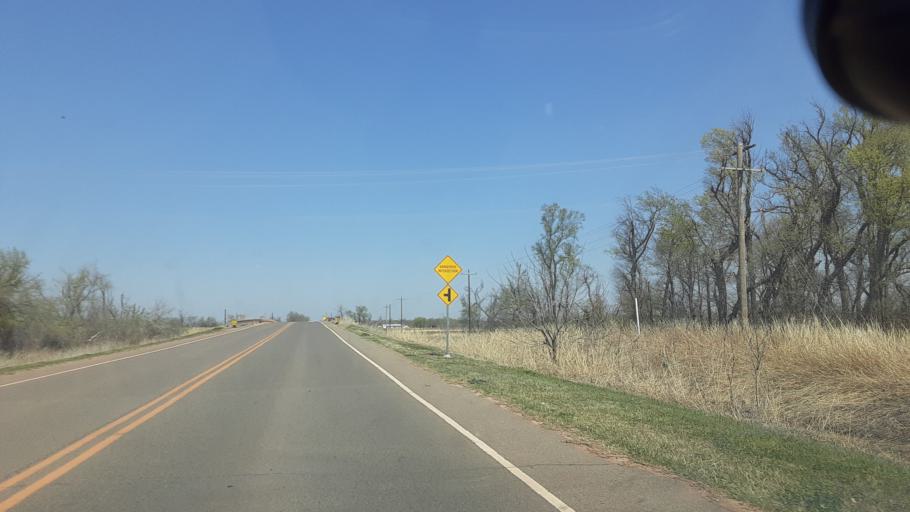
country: US
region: Oklahoma
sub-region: Logan County
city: Guthrie
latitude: 35.8124
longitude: -97.4784
